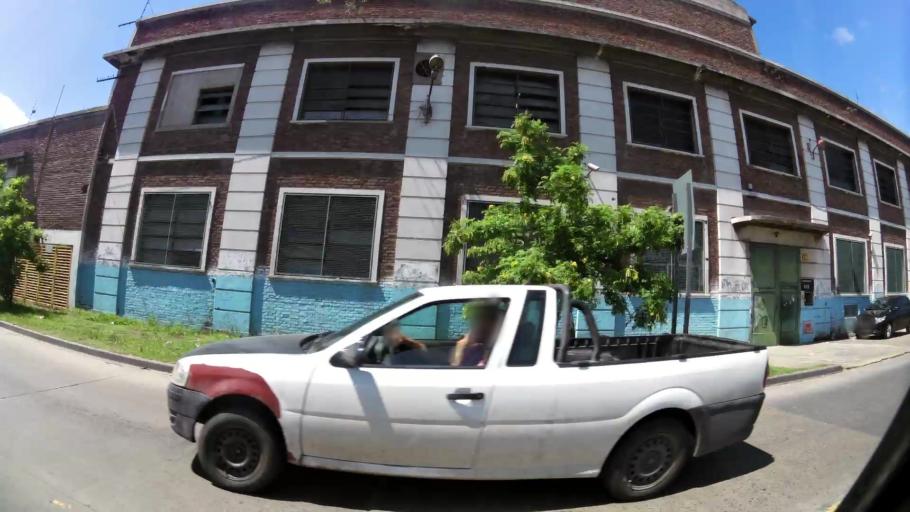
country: AR
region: Buenos Aires
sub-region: Partido de Lanus
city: Lanus
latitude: -34.6605
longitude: -58.4182
